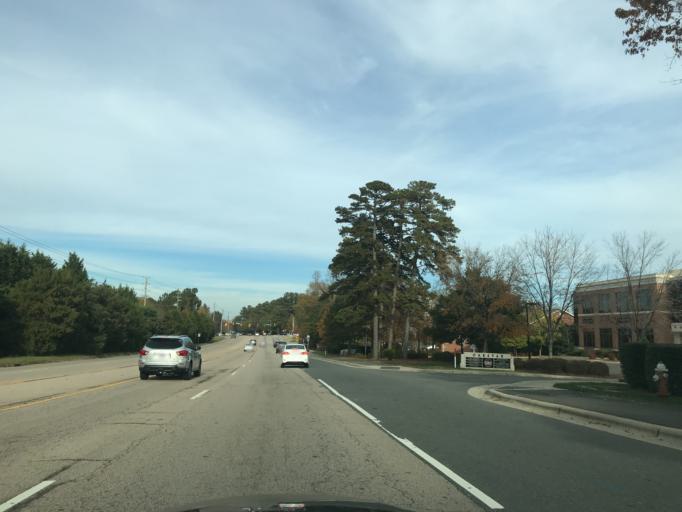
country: US
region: North Carolina
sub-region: Wake County
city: Wake Forest
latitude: 35.9010
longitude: -78.6059
